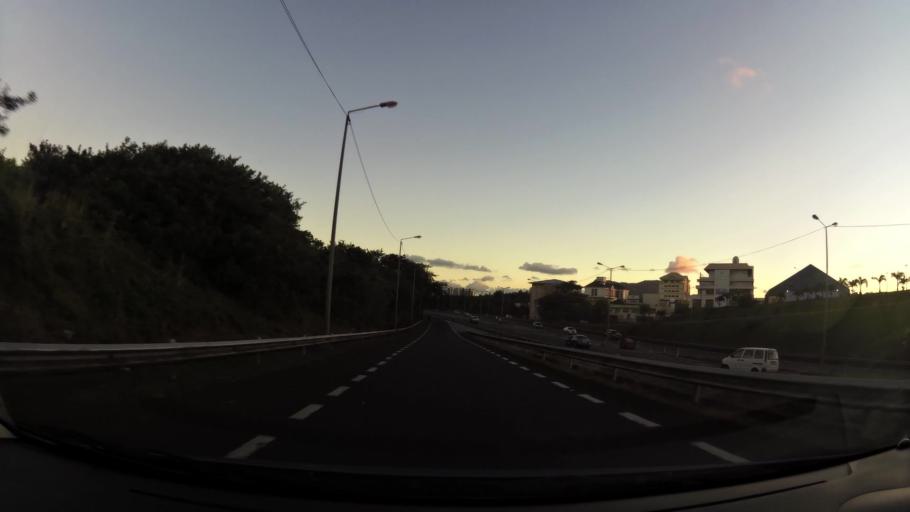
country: MU
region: Moka
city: Moka
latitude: -20.2328
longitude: 57.5009
